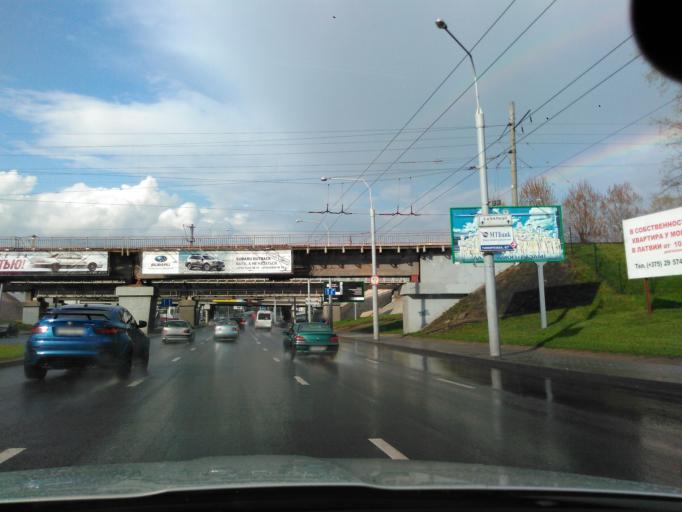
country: BY
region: Minsk
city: Minsk
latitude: 53.9254
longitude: 27.5051
